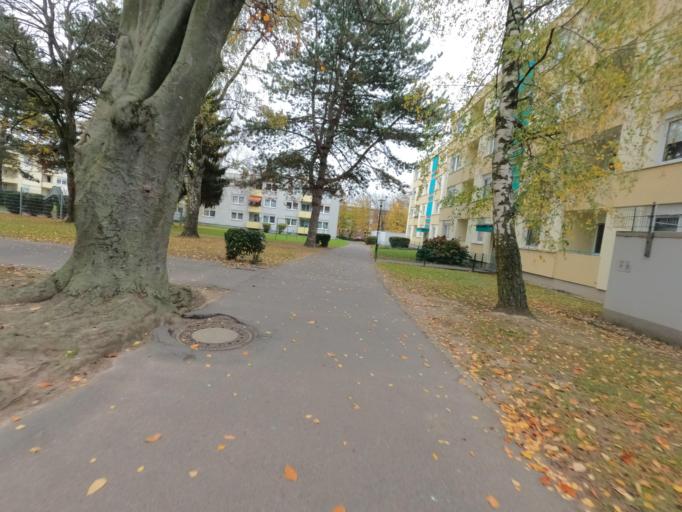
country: DE
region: North Rhine-Westphalia
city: Geilenkirchen
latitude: 50.9710
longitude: 6.1142
